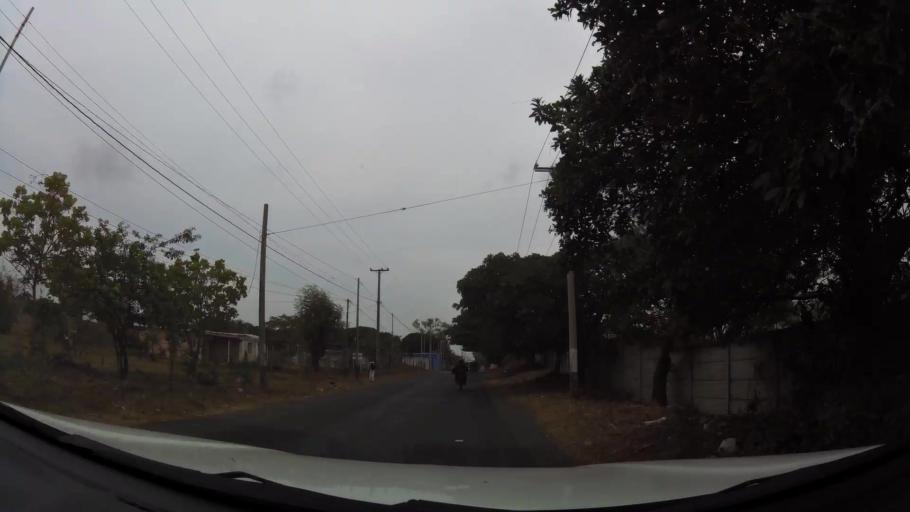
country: NI
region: Masaya
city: Ticuantepe
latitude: 12.0703
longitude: -86.1831
